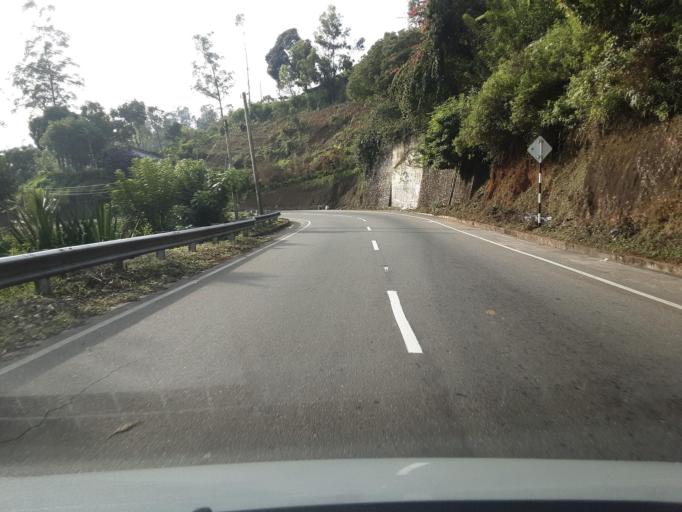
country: LK
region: Uva
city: Badulla
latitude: 6.9379
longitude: 80.9949
